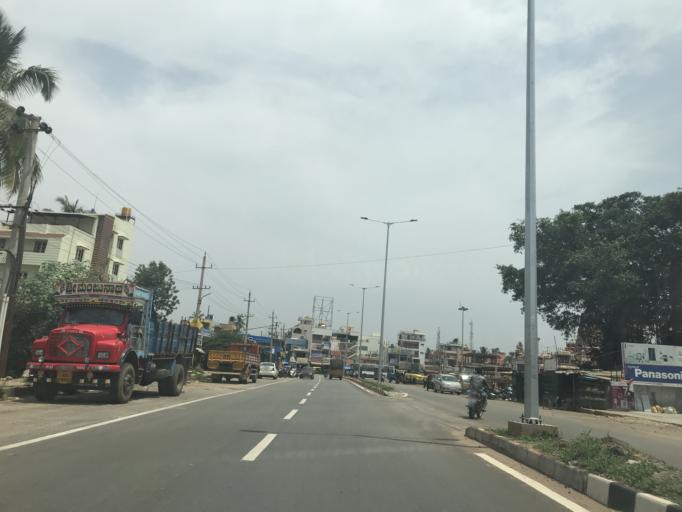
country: IN
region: Karnataka
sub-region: Bangalore Urban
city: Yelahanka
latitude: 13.1357
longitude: 77.6684
